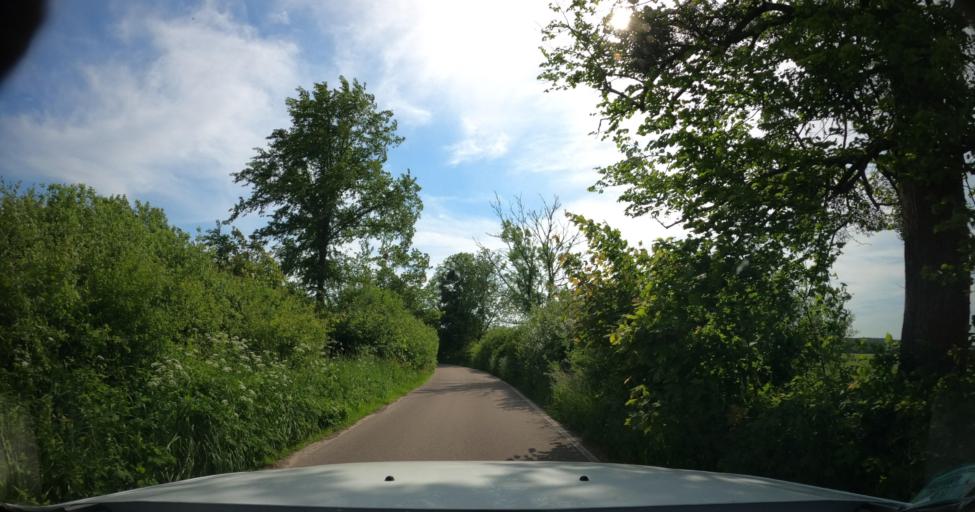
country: PL
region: Warmian-Masurian Voivodeship
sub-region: Powiat ostrodzki
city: Milakowo
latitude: 54.0200
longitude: 20.1599
